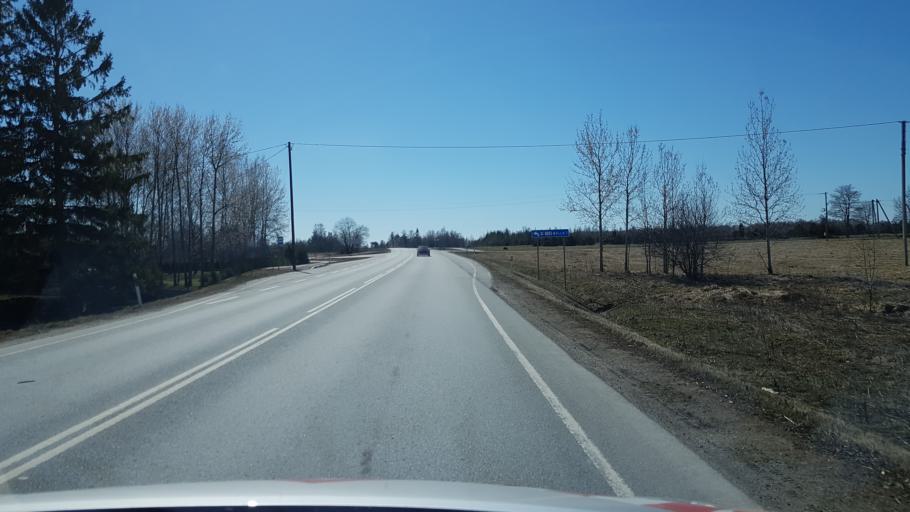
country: EE
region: Laeaene-Virumaa
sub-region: Viru-Nigula vald
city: Kunda
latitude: 59.4820
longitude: 26.4902
